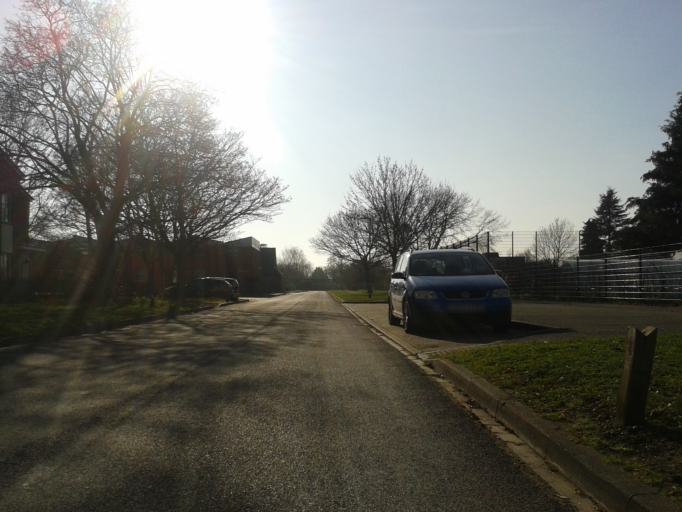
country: GB
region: England
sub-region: Cambridgeshire
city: Histon
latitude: 52.2315
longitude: 0.1305
